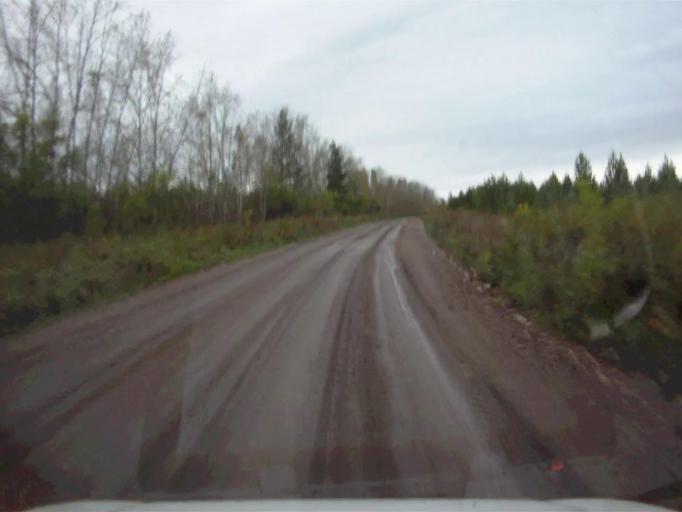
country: RU
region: Chelyabinsk
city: Nyazepetrovsk
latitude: 56.1357
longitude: 59.3030
